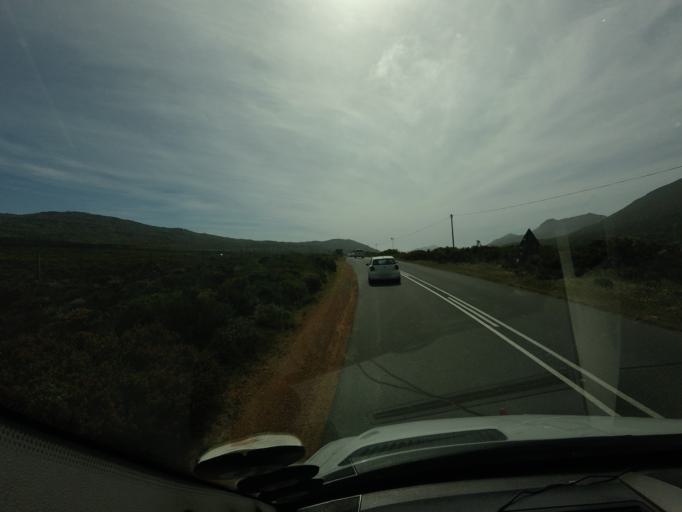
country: ZA
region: Western Cape
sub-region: City of Cape Town
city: Retreat
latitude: -34.2580
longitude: 18.4577
